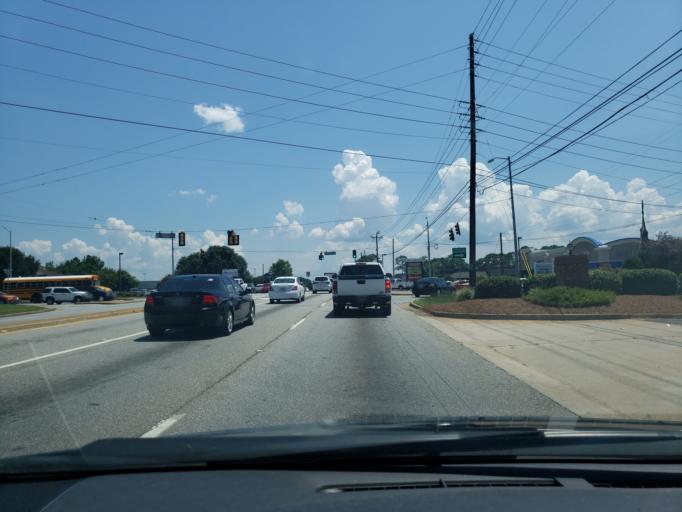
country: US
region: Georgia
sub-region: Dougherty County
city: Albany
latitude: 31.6181
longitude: -84.2227
